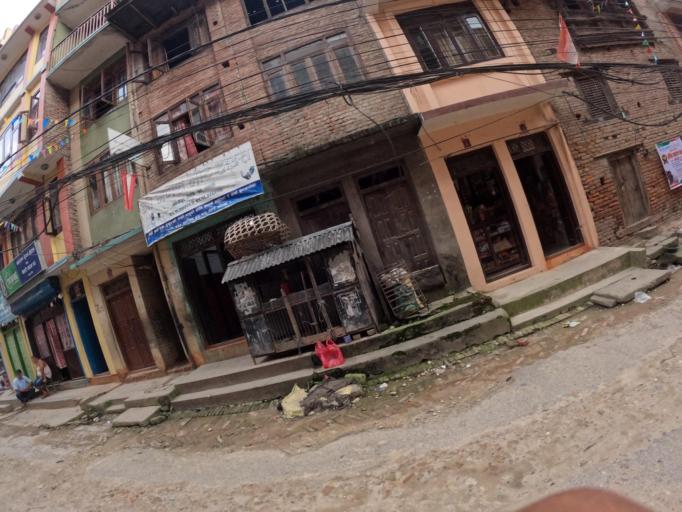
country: NP
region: Central Region
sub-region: Bagmati Zone
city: Bhaktapur
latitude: 27.6807
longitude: 85.3860
